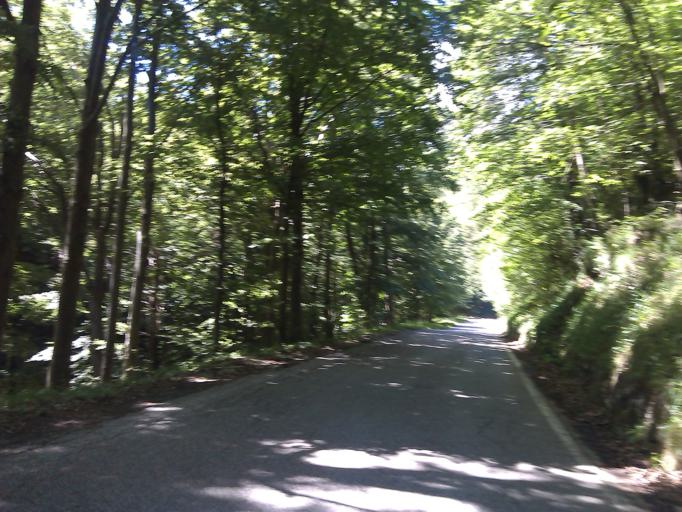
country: IT
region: Tuscany
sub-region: Provincia di Prato
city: Cantagallo
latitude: 44.0163
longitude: 11.0280
